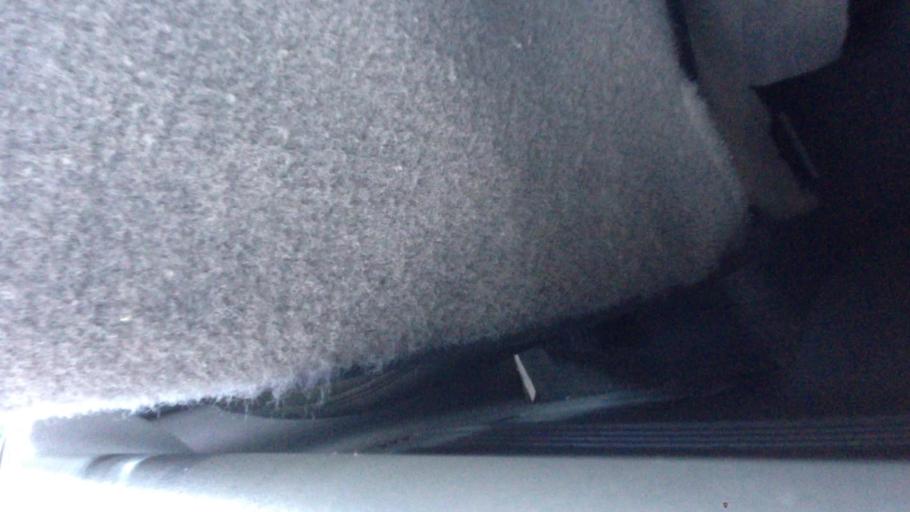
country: US
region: New York
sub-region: Greene County
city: Catskill
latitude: 42.1317
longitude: -73.8204
